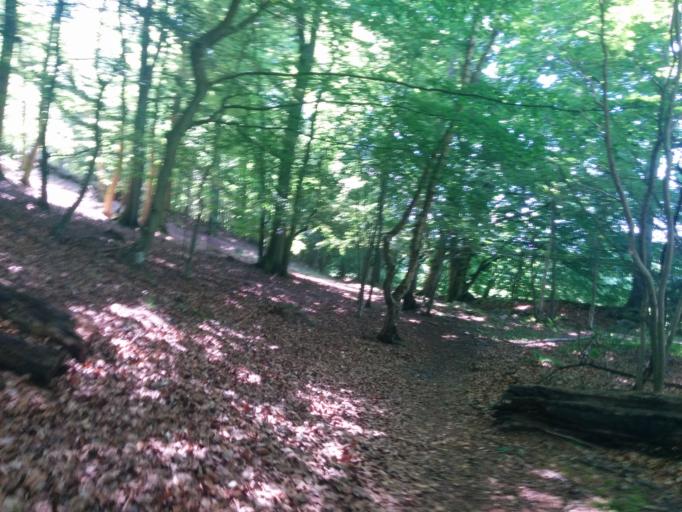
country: SE
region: Skane
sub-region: Lunds Kommun
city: Genarp
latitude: 55.5889
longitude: 13.3875
